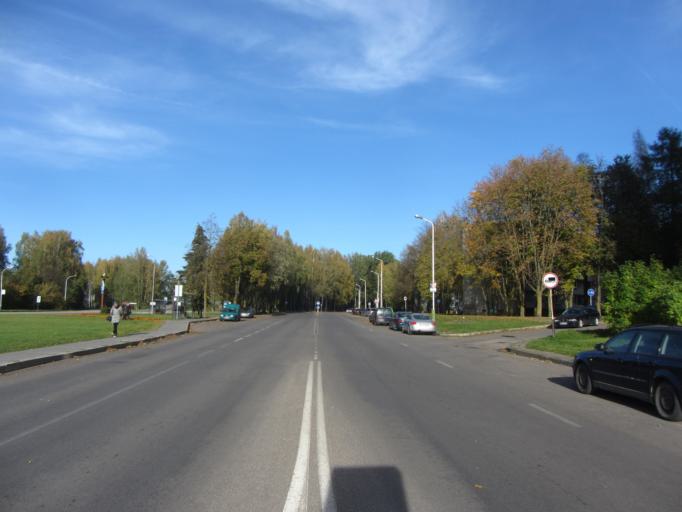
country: LT
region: Vilnius County
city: Elektrenai
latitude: 54.7877
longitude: 24.6584
